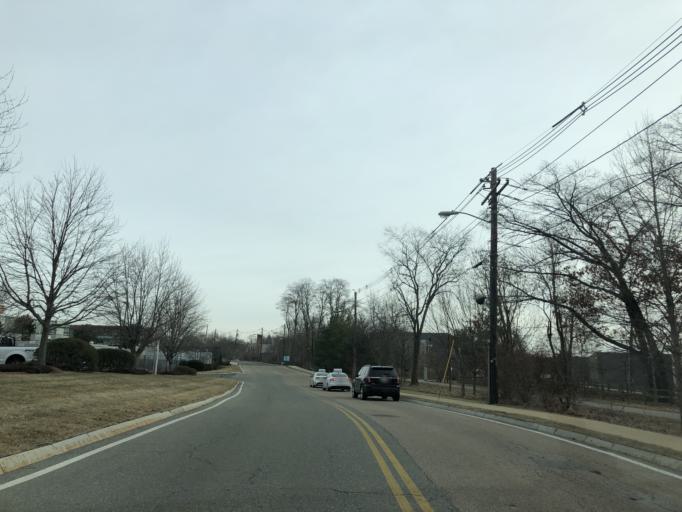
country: US
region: Massachusetts
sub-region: Middlesex County
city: Watertown
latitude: 42.3650
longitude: -71.1597
